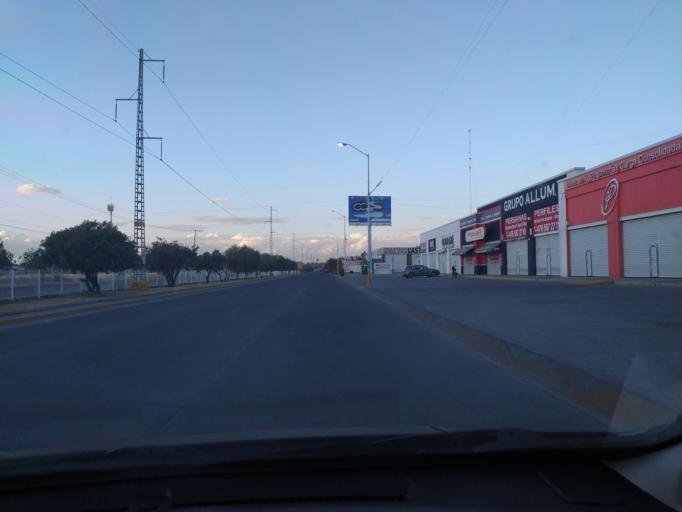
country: LA
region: Oudomxai
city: Muang La
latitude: 21.0220
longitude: 101.8694
